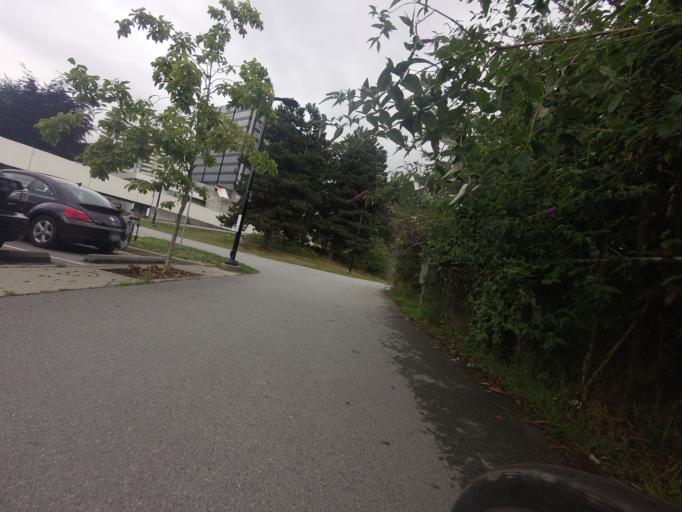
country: CA
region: British Columbia
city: West End
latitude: 49.3245
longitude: -123.1346
